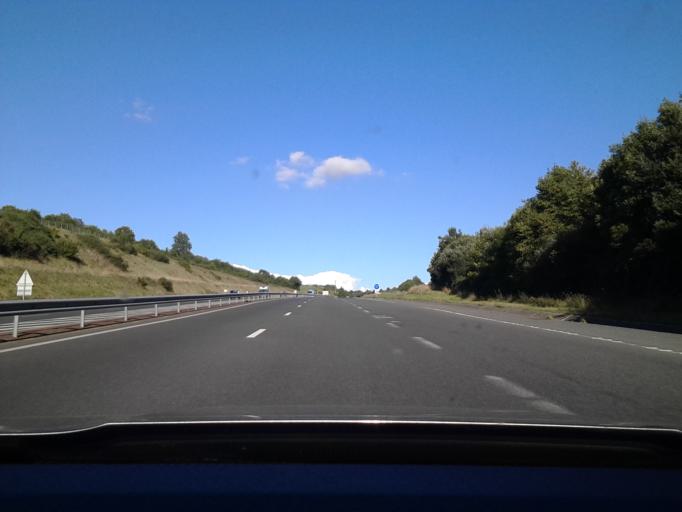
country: FR
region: Lower Normandy
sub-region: Departement de la Manche
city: Tessy-sur-Vire
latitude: 48.9472
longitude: -1.0245
